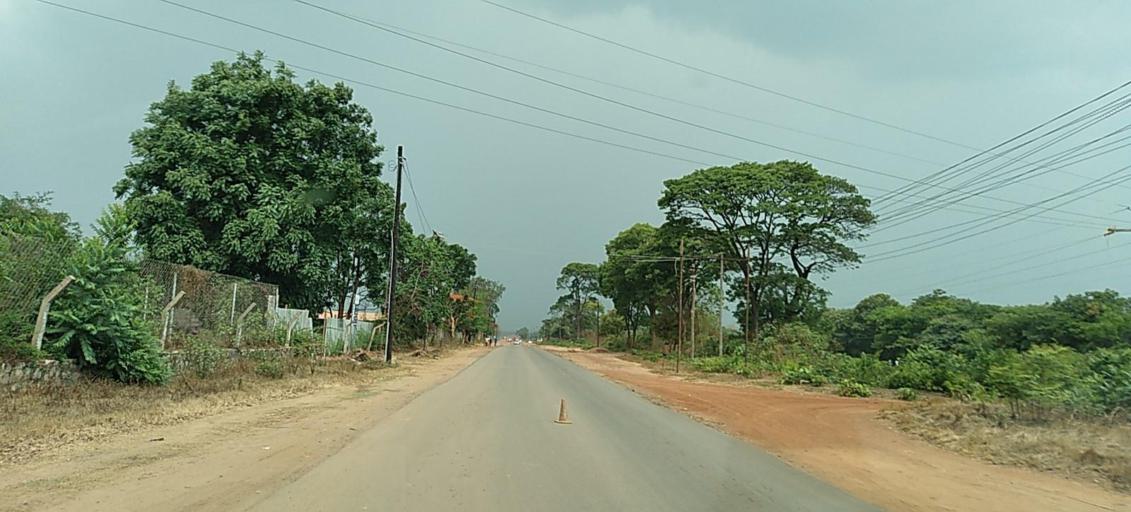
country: ZM
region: Copperbelt
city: Kalulushi
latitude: -12.8330
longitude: 28.1052
